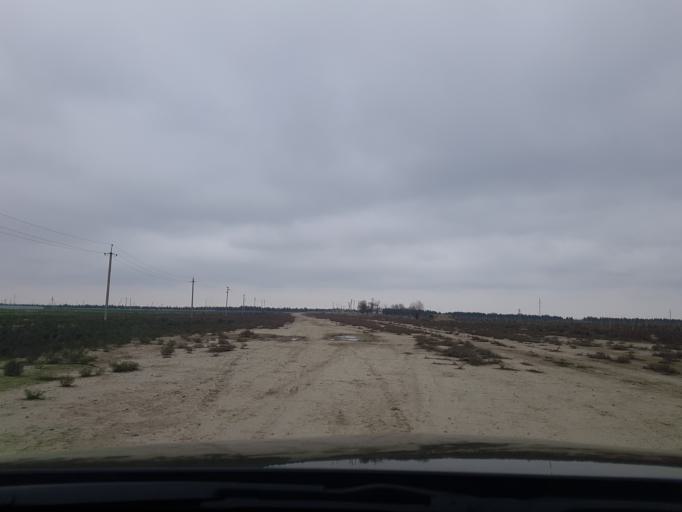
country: TM
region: Ahal
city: Abadan
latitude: 38.1416
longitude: 57.9792
